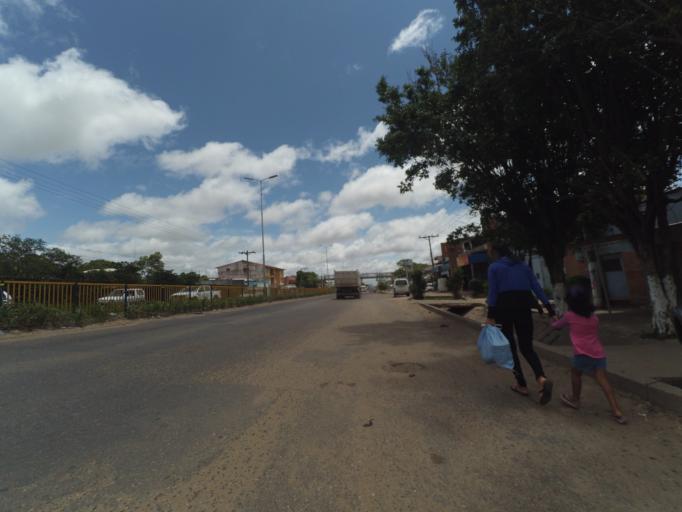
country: BO
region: Santa Cruz
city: Santa Cruz de la Sierra
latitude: -17.8501
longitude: -63.2514
